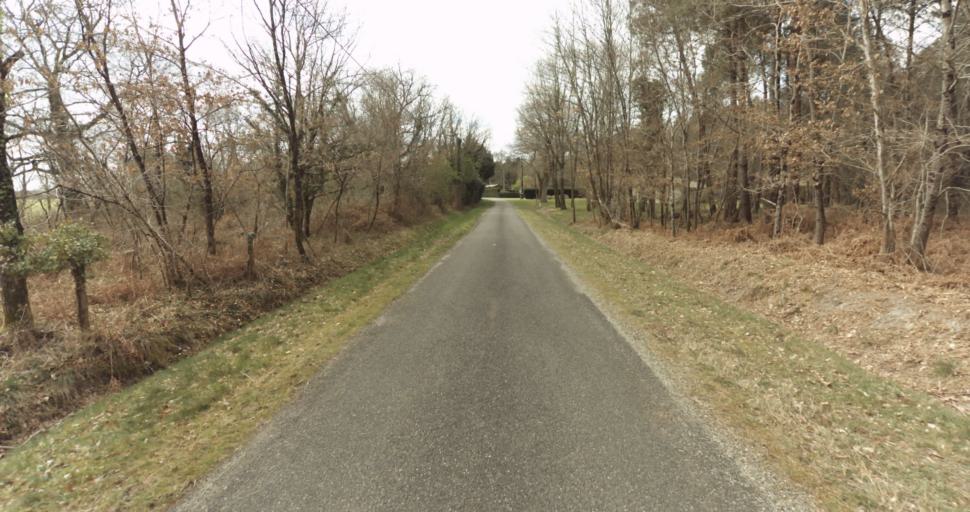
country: FR
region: Aquitaine
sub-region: Departement des Landes
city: Roquefort
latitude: 44.0706
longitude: -0.3954
